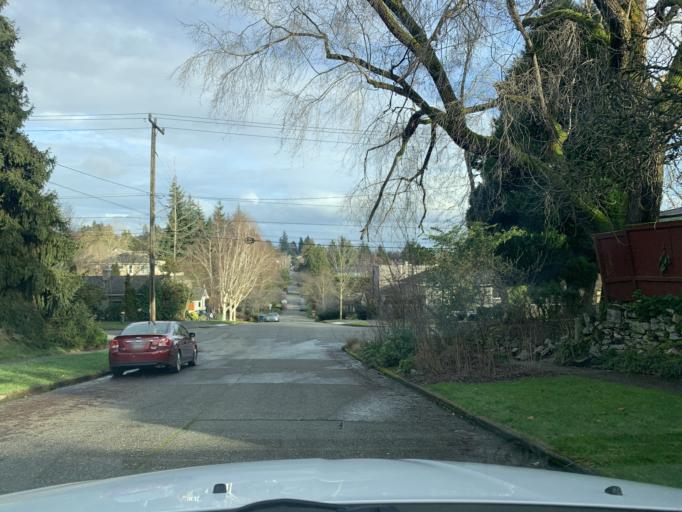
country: US
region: Washington
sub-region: King County
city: Yarrow Point
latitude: 47.6703
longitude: -122.2874
